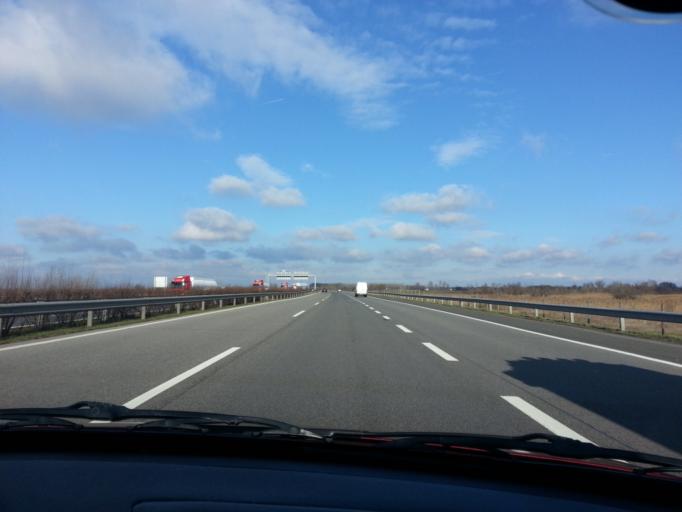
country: HU
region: Csongrad
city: Szatymaz
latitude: 46.3076
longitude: 20.0416
